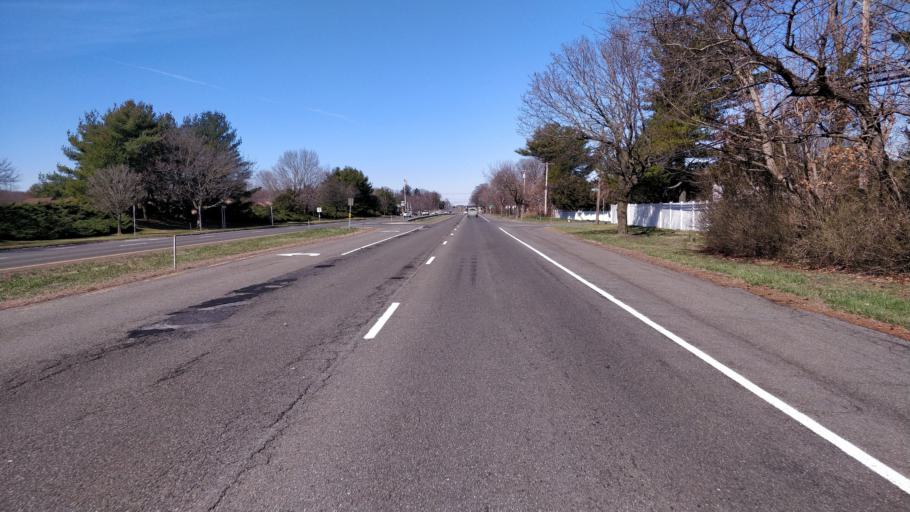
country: US
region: New York
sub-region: Suffolk County
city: Commack
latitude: 40.8369
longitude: -73.2727
